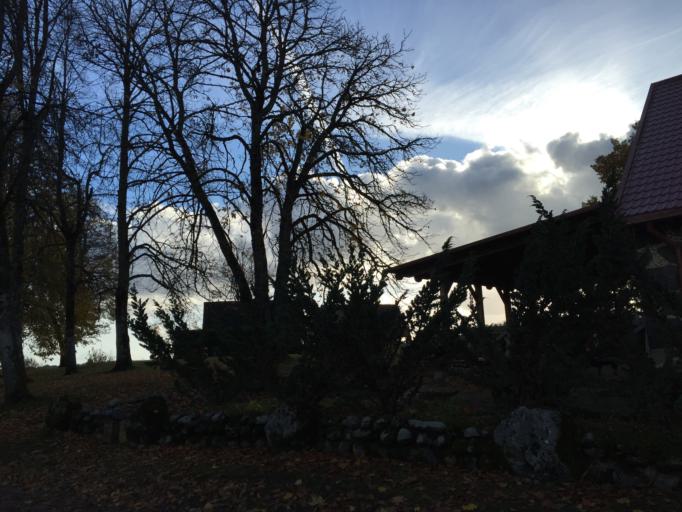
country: LV
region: Ogre
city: Jumprava
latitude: 56.7685
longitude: 24.9748
